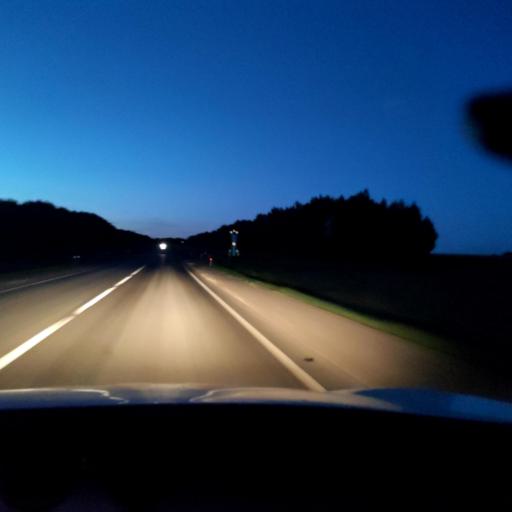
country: RU
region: Tatarstan
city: Rybnaya Sloboda
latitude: 55.4549
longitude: 49.9326
